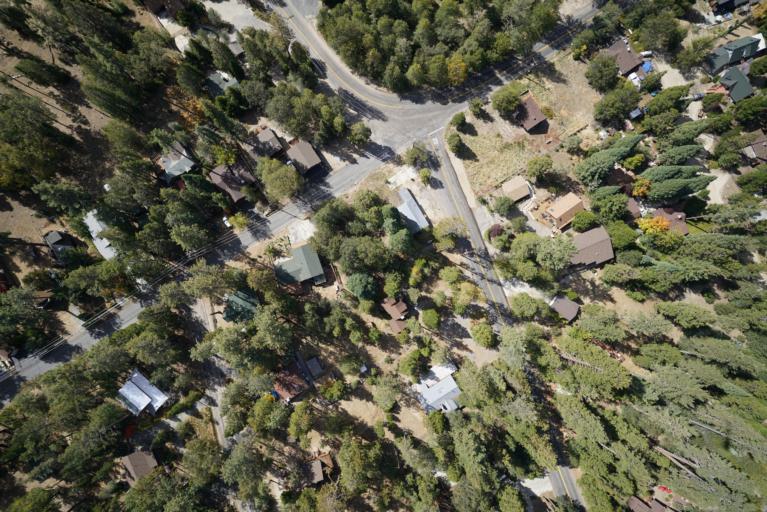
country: US
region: California
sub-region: Riverside County
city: Idyllwild
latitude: 33.7525
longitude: -116.7025
